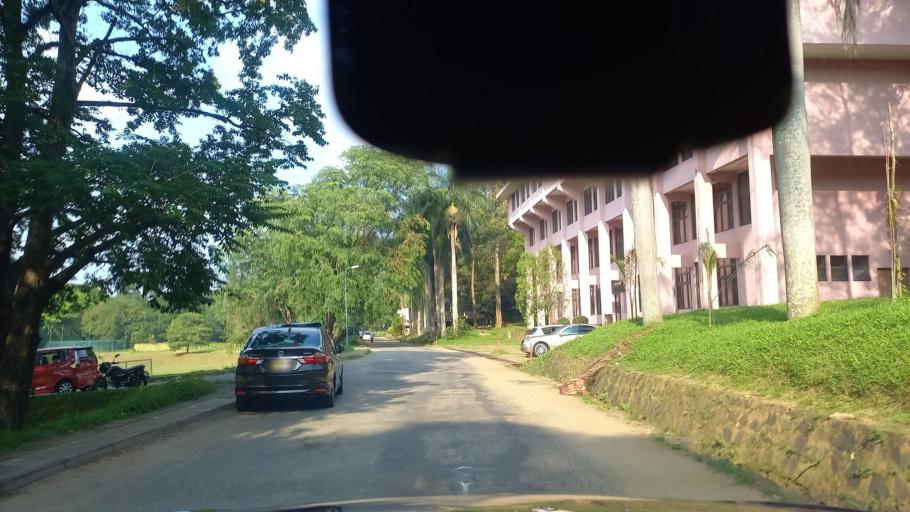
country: LK
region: Central
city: Kandy
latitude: 7.2586
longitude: 80.5983
